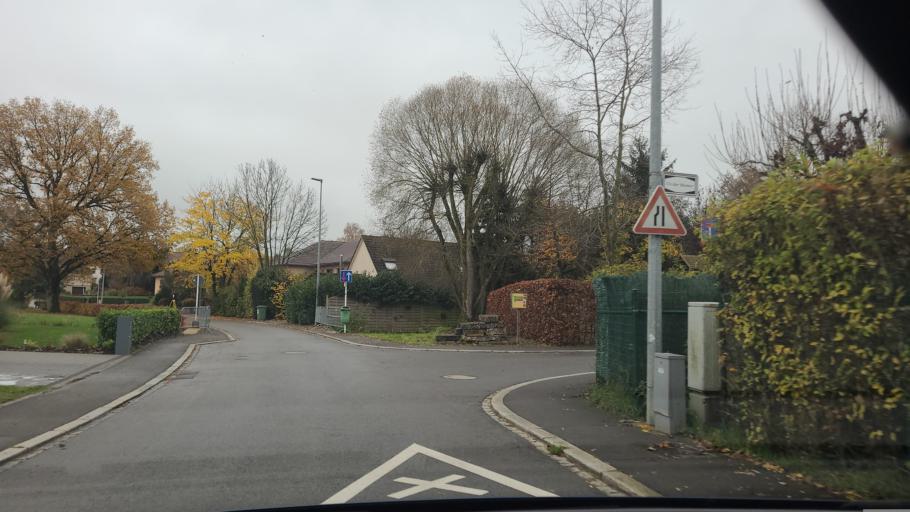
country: LU
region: Luxembourg
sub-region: Canton de Capellen
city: Garnich
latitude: 49.6127
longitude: 5.9523
